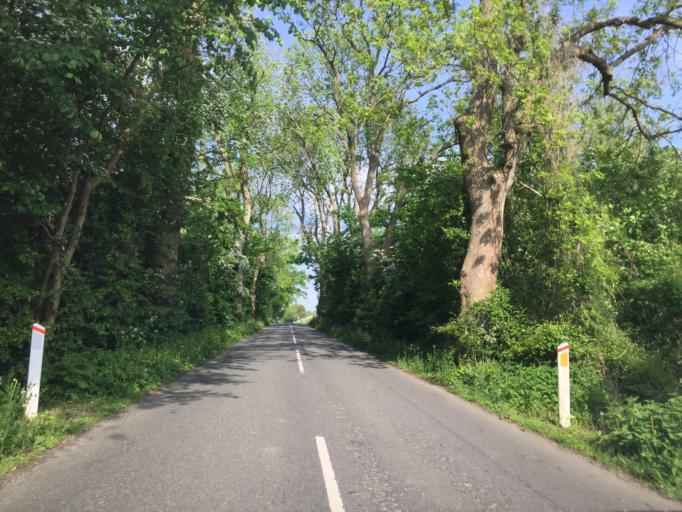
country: DK
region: South Denmark
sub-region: Svendborg Kommune
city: Thuro By
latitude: 55.1411
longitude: 10.7633
